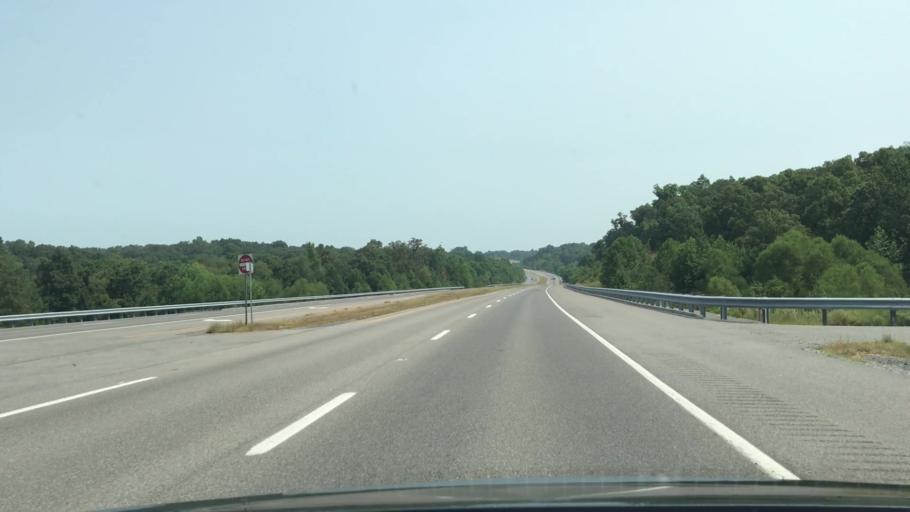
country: US
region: Kentucky
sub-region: Calloway County
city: Murray
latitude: 36.7502
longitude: -88.1576
